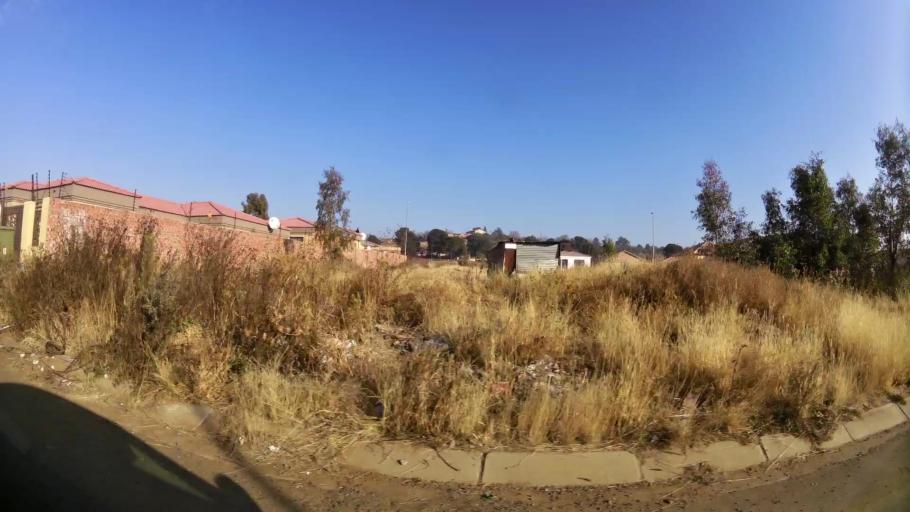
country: ZA
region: Orange Free State
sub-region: Mangaung Metropolitan Municipality
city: Bloemfontein
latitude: -29.1597
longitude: 26.2071
